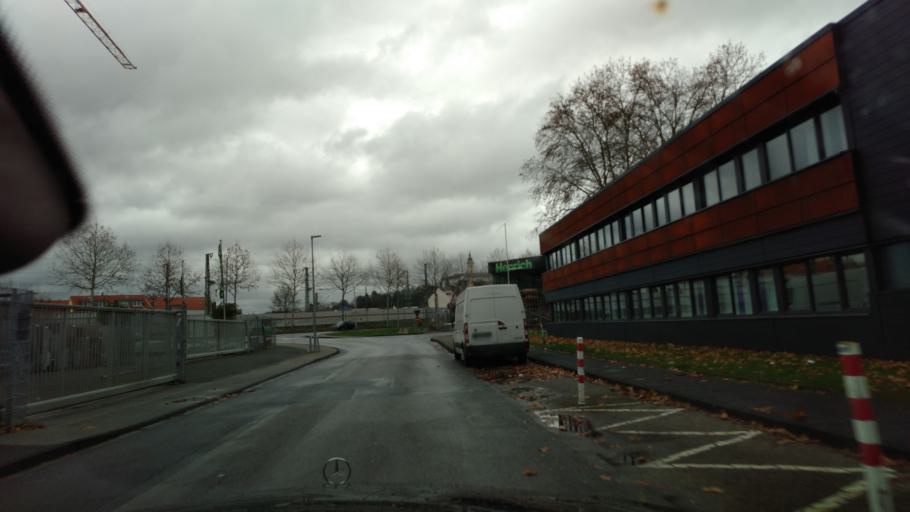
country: DE
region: North Rhine-Westphalia
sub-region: Regierungsbezirk Koln
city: Siegburg
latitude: 50.7968
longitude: 7.1966
